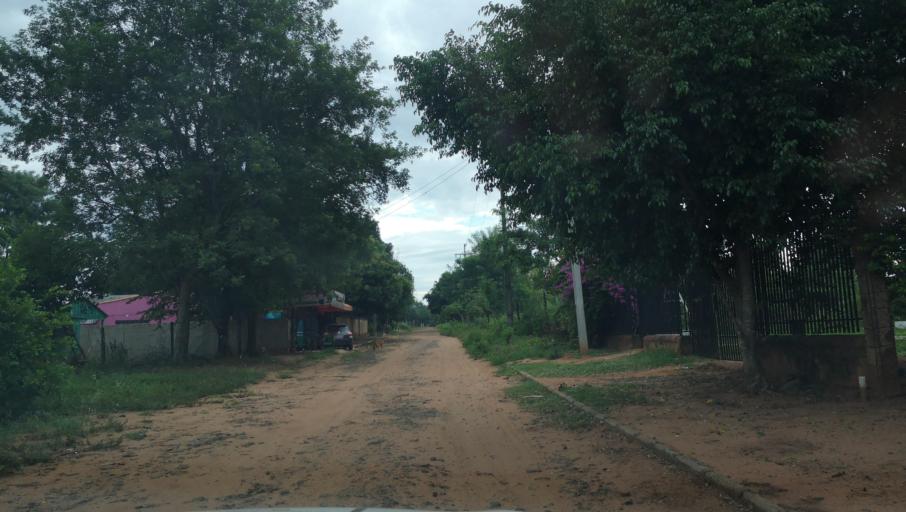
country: PY
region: San Pedro
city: Capiibary
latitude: -24.7239
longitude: -56.0183
